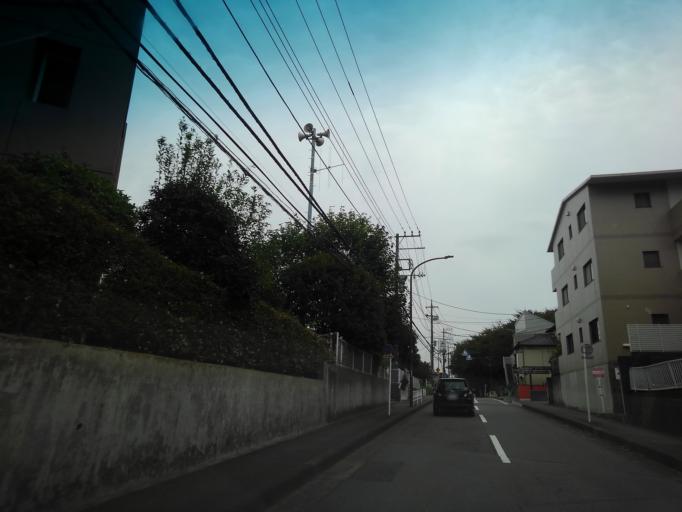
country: JP
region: Tokyo
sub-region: Machida-shi
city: Machida
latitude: 35.5768
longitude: 139.3989
